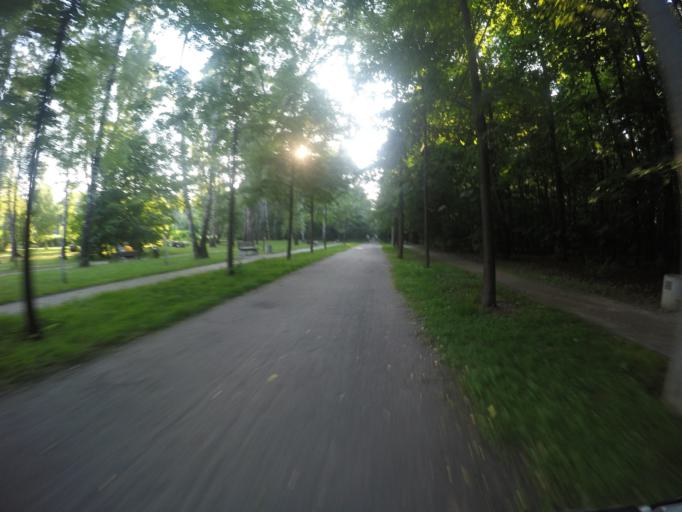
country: RU
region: Moscow
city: Sokol'niki
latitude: 55.7987
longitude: 37.6660
